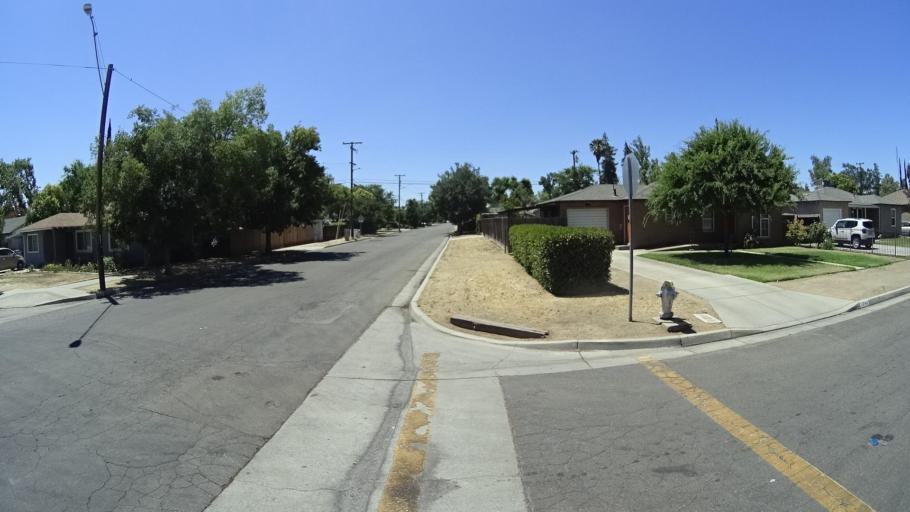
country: US
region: California
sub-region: Fresno County
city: Fresno
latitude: 36.7923
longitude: -119.7951
